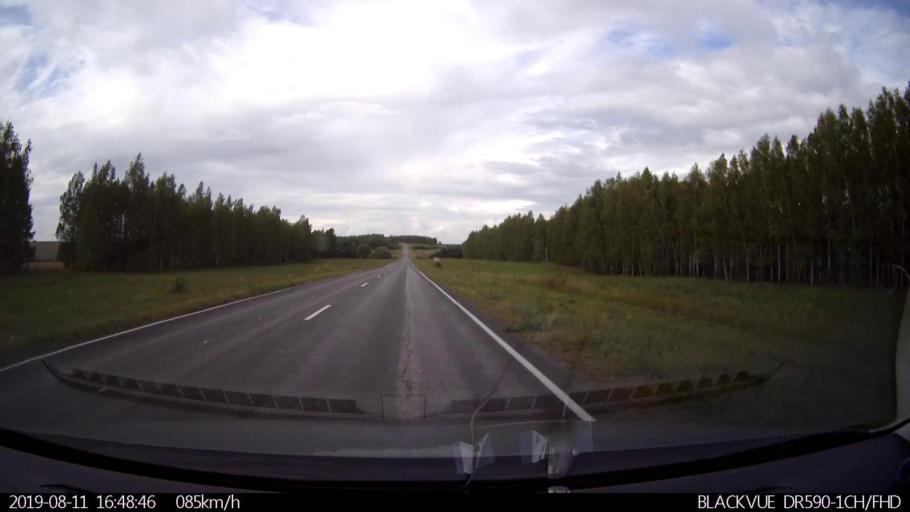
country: RU
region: Ulyanovsk
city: Mayna
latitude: 54.2130
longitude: 47.6935
